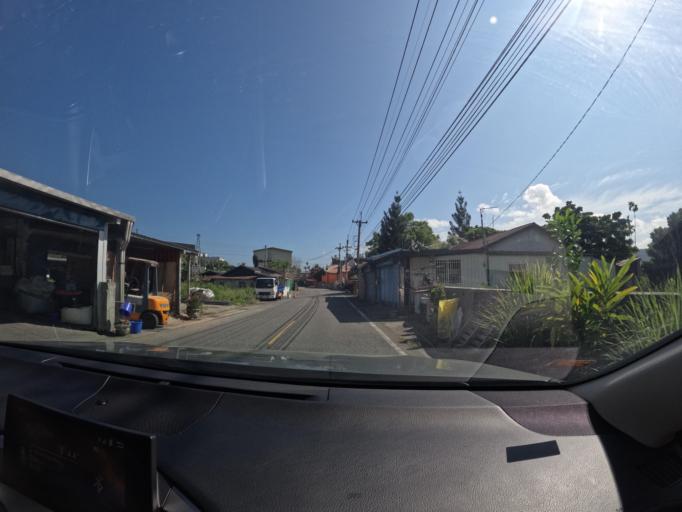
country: TW
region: Taiwan
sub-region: Hualien
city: Hualian
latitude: 23.5760
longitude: 121.3750
